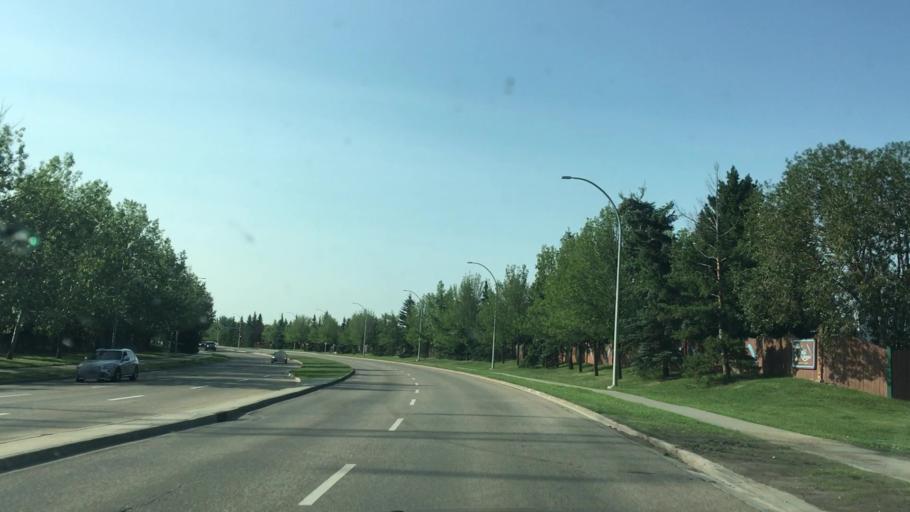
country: CA
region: Alberta
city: Edmonton
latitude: 53.4615
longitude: -113.5389
